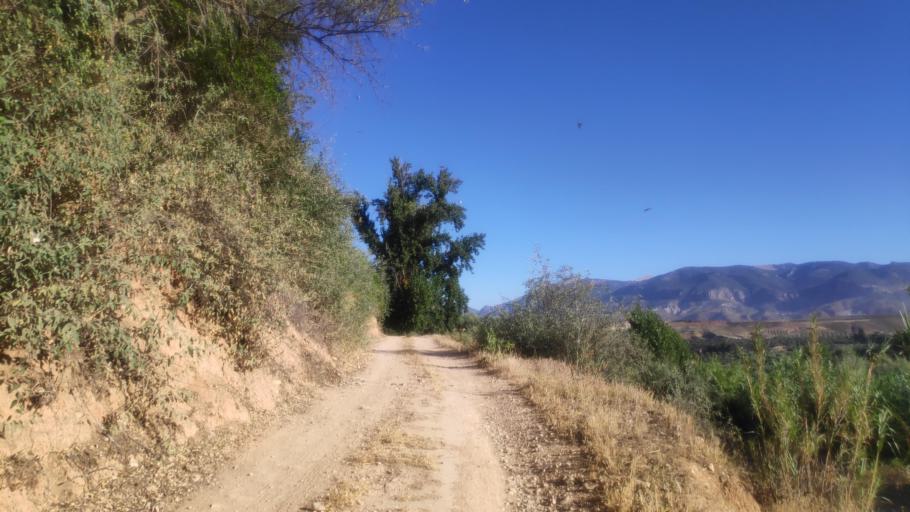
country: ES
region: Andalusia
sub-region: Provincia de Jaen
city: Hinojares
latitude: 37.6764
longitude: -2.9740
